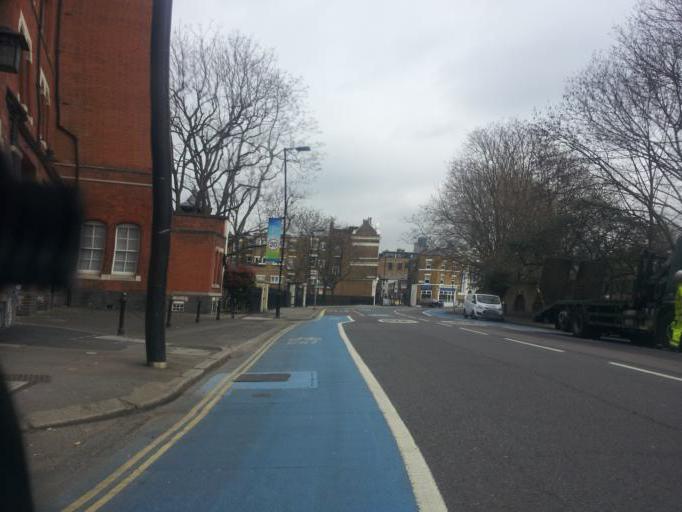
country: GB
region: England
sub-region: Greater London
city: City of London
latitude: 51.5020
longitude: -0.0978
